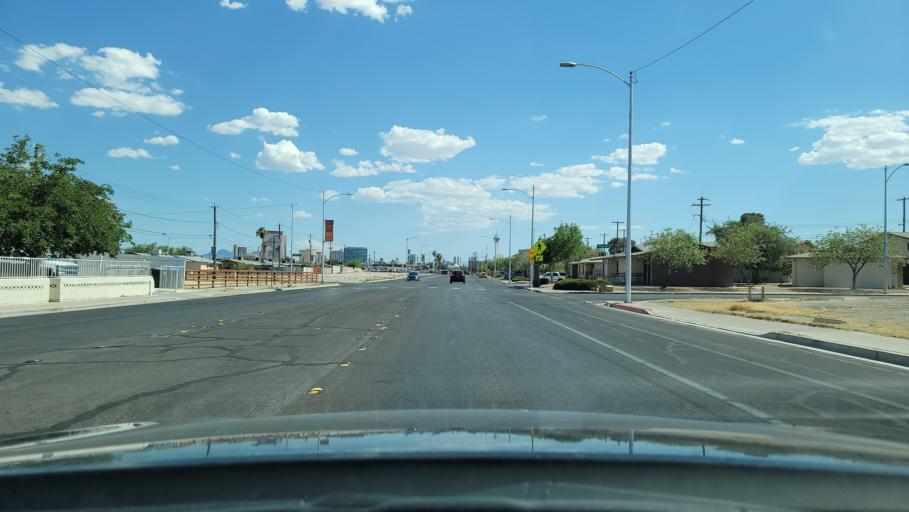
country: US
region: Nevada
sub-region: Clark County
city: Las Vegas
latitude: 36.1924
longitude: -115.1519
